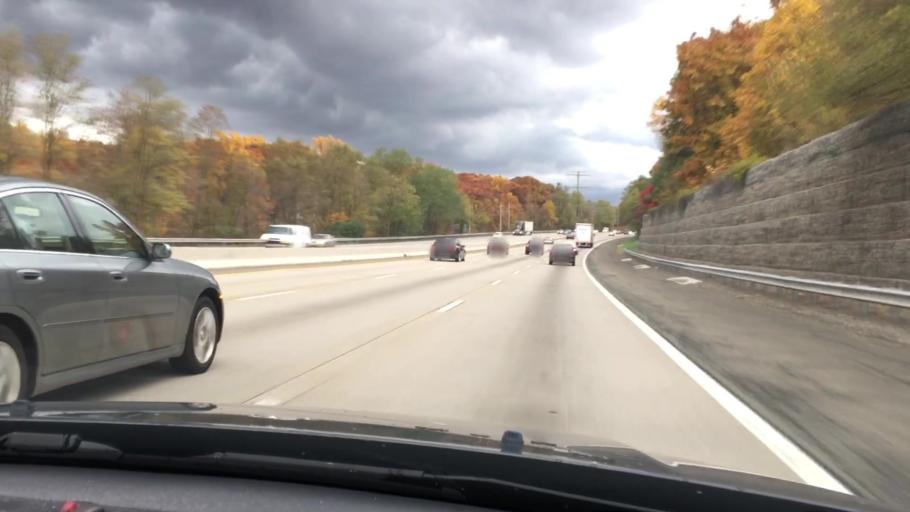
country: US
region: New Jersey
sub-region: Morris County
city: Boonton
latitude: 40.9247
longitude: -74.3604
